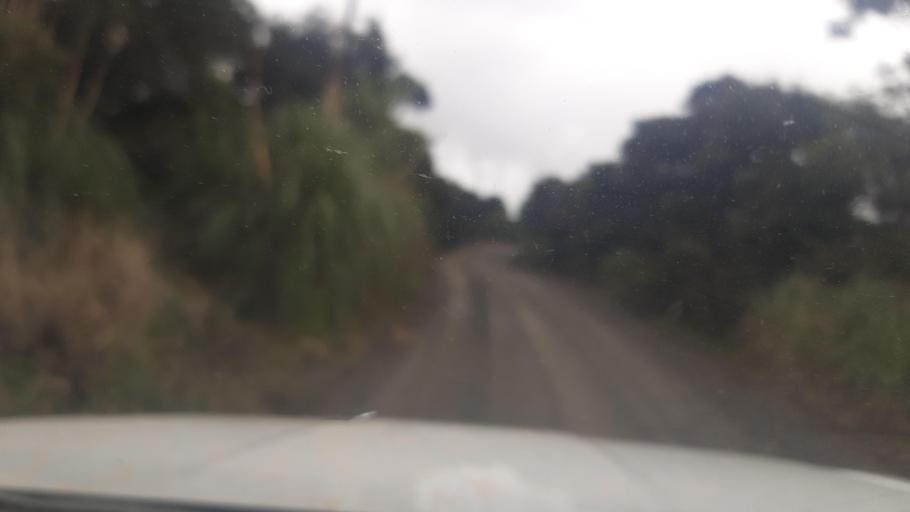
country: NZ
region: Northland
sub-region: Far North District
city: Taipa
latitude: -35.0616
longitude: 173.5328
